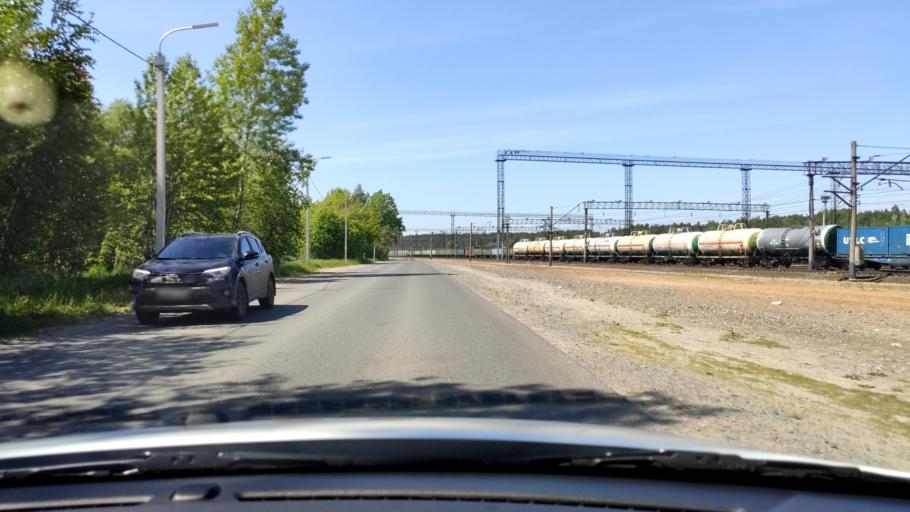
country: RU
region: Tatarstan
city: Osinovo
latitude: 55.8195
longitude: 48.8598
